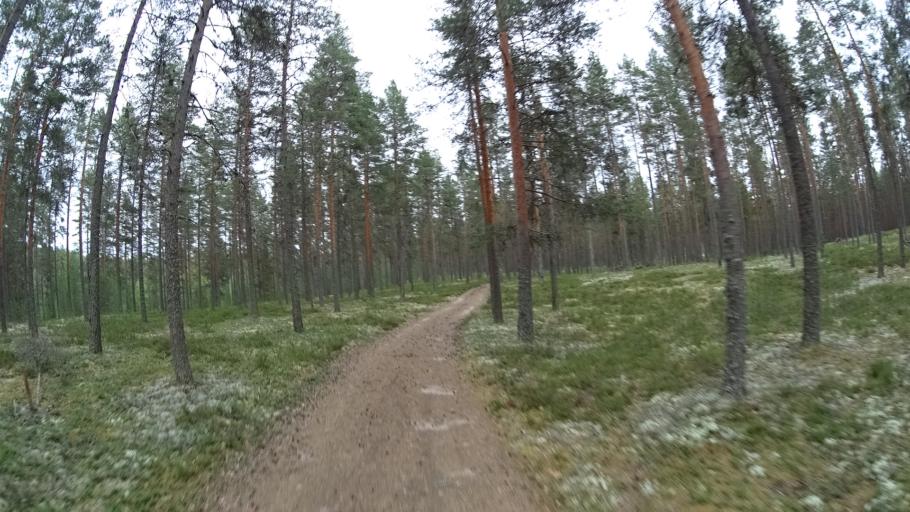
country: FI
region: Satakunta
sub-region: Pohjois-Satakunta
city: Jaemijaervi
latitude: 61.7630
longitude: 22.7534
